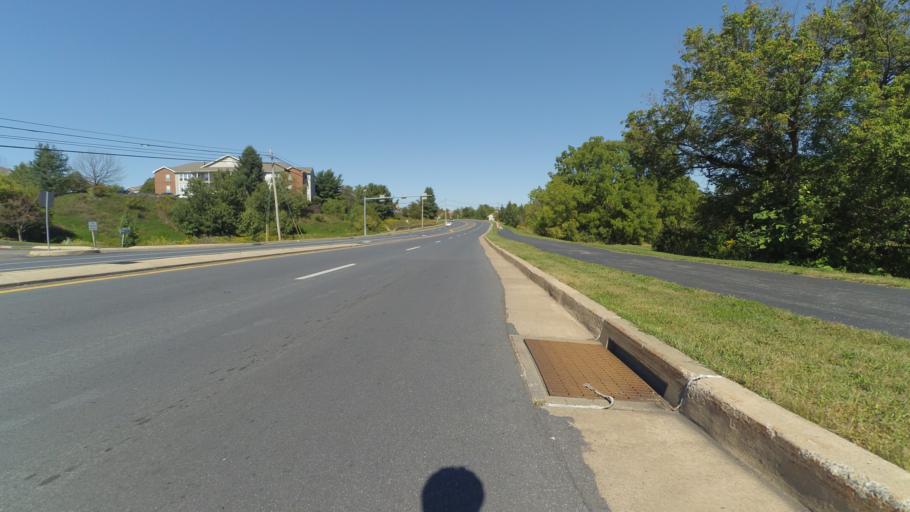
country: US
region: Pennsylvania
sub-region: Centre County
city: State College
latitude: 40.7979
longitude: -77.8872
